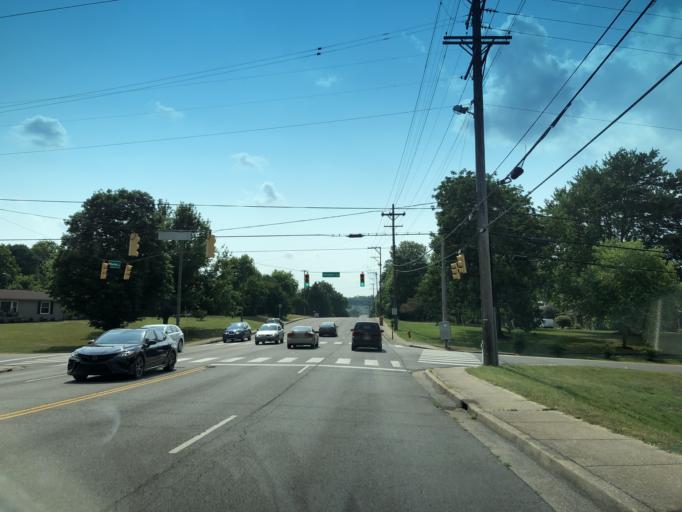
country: US
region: Tennessee
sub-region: Davidson County
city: Goodlettsville
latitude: 36.2486
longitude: -86.7282
